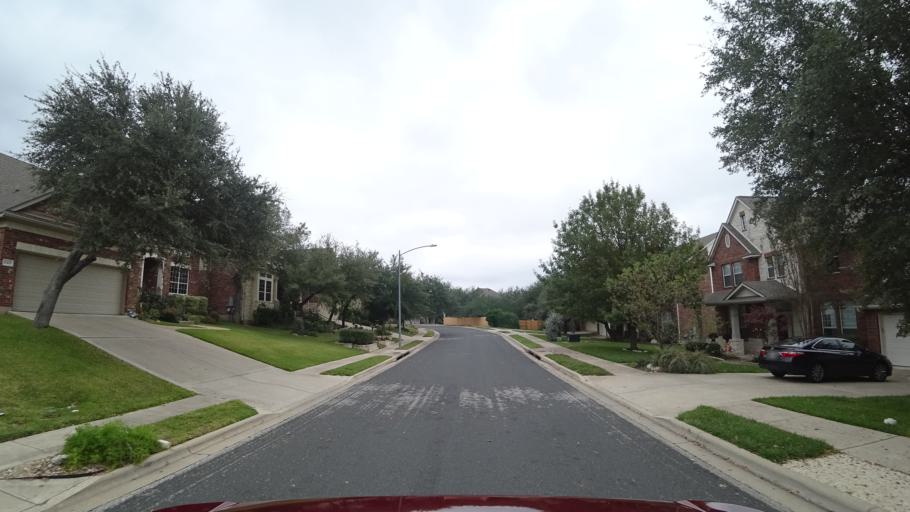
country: US
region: Texas
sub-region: Williamson County
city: Anderson Mill
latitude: 30.4298
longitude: -97.8189
